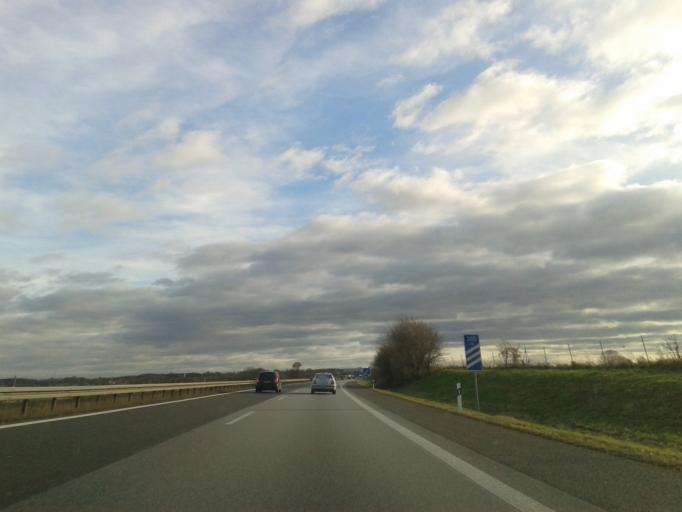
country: DE
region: Saxony
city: Goda
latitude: 51.2020
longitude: 14.3185
